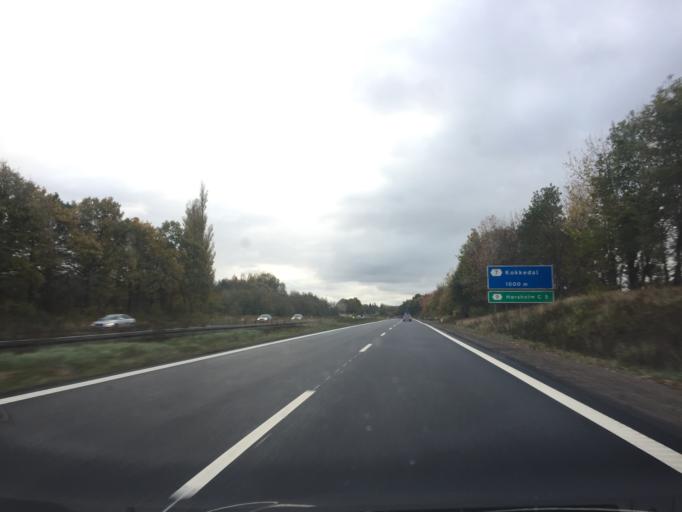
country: DK
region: Capital Region
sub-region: Fredensborg Kommune
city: Kokkedal
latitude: 55.9220
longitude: 12.4746
